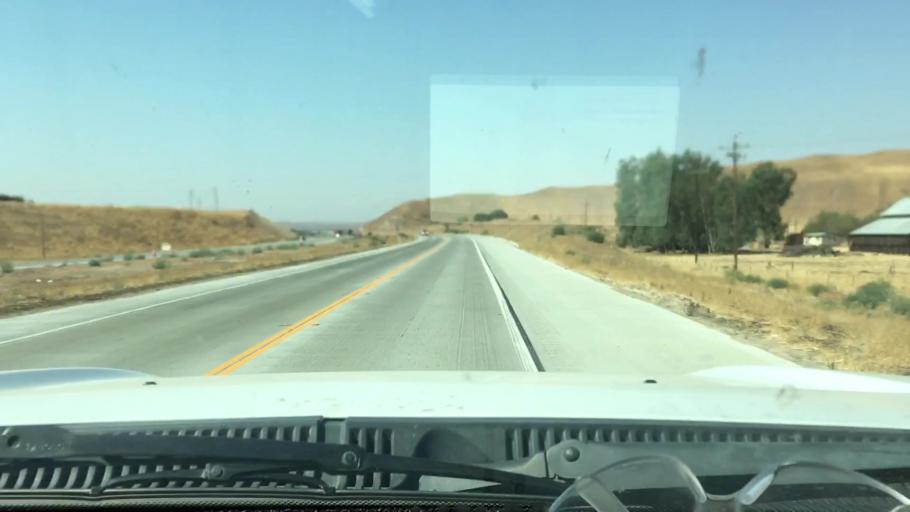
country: US
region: California
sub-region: San Luis Obispo County
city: Shandon
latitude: 35.6725
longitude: -120.3531
